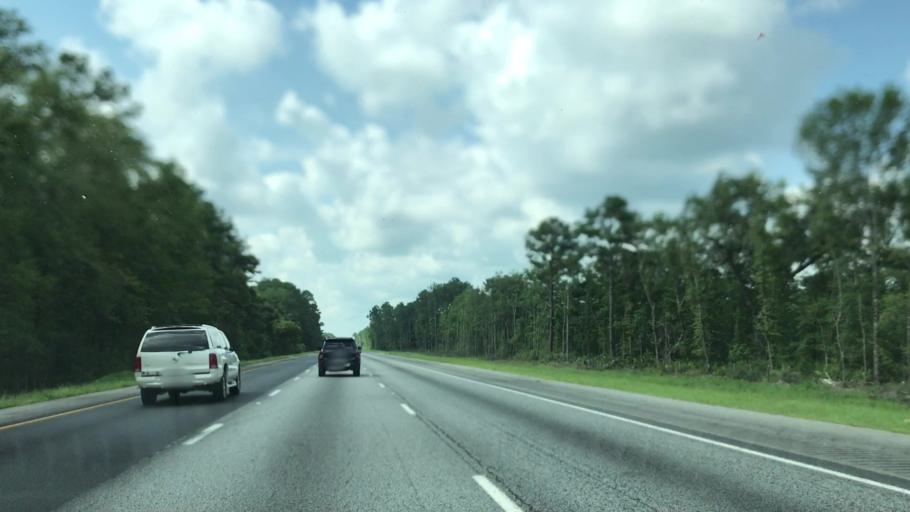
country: US
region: Georgia
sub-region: Camden County
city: Woodbine
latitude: 30.9222
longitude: -81.6865
